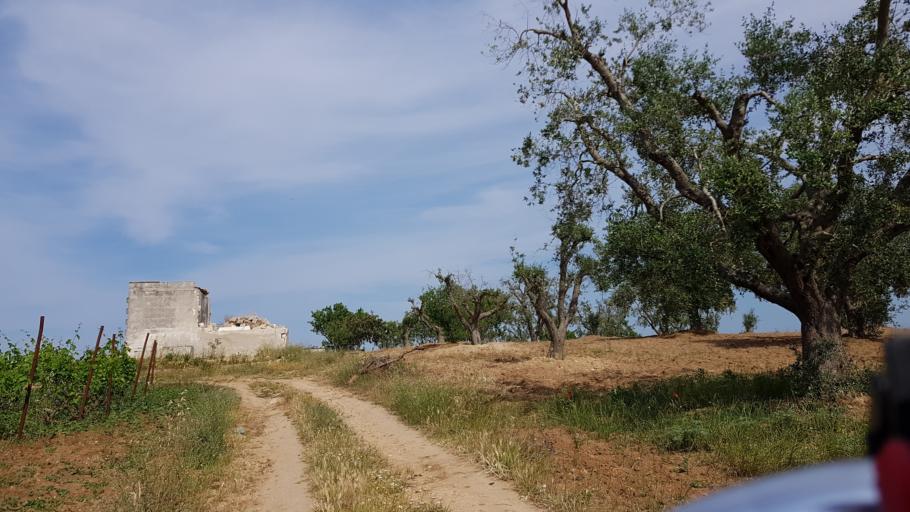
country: IT
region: Apulia
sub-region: Provincia di Brindisi
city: San Vito dei Normanni
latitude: 40.6595
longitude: 17.8000
